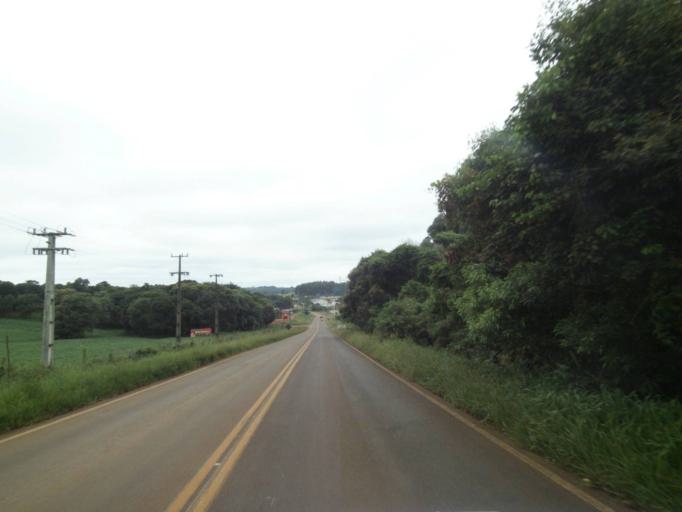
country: BR
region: Parana
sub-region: Pitanga
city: Pitanga
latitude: -24.9228
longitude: -51.8709
